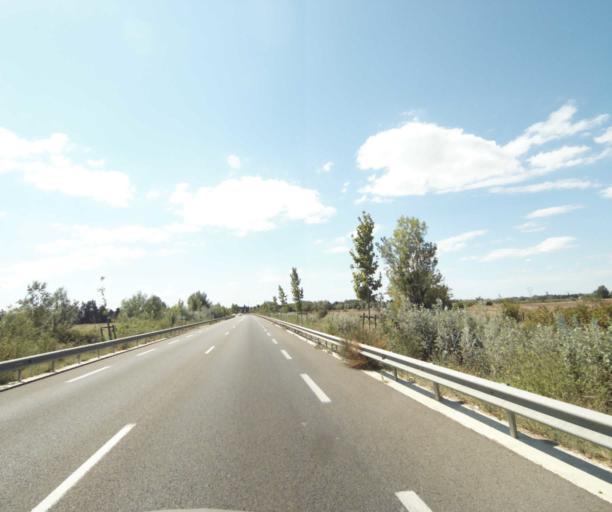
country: FR
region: Languedoc-Roussillon
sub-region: Departement du Gard
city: Rodilhan
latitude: 43.8153
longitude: 4.4137
